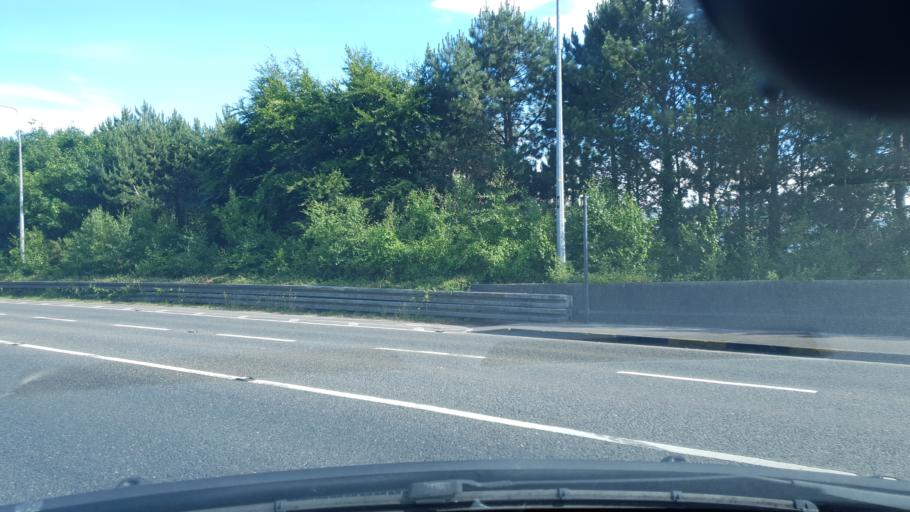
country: IE
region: Munster
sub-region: Ciarrai
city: Cill Airne
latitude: 52.0695
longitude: -9.5050
